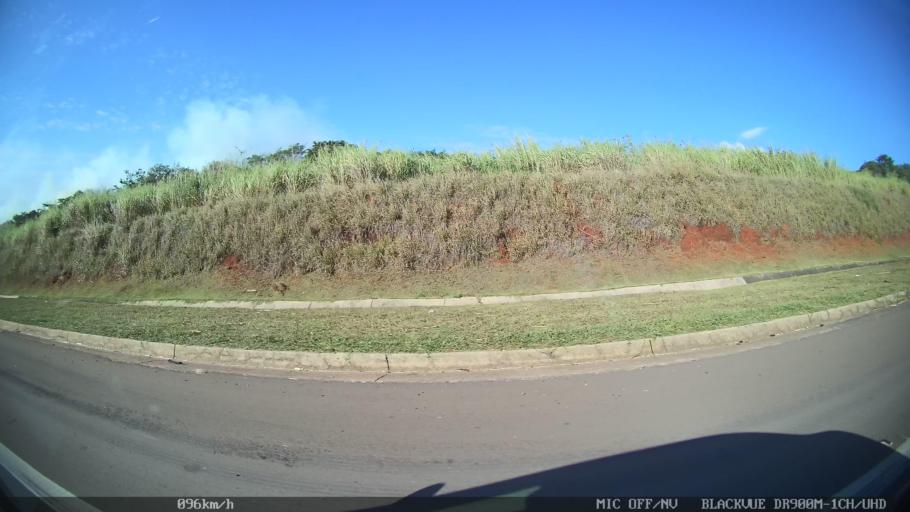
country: BR
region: Sao Paulo
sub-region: Piracicaba
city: Piracicaba
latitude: -22.7058
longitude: -47.6116
